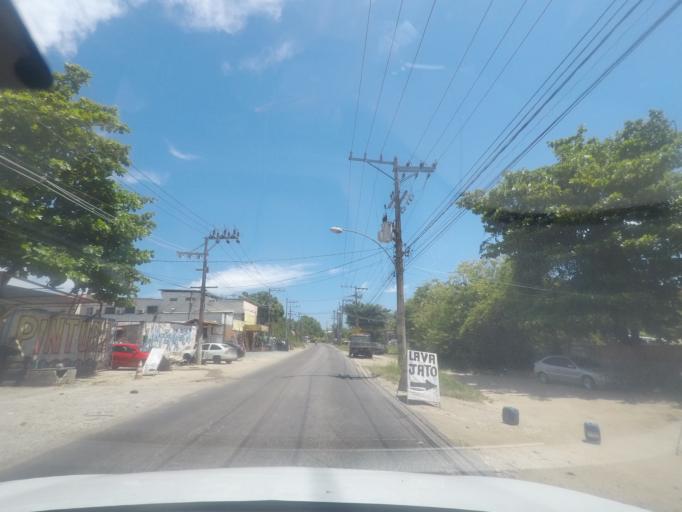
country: BR
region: Rio de Janeiro
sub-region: Itaguai
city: Itaguai
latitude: -22.9947
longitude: -43.6504
